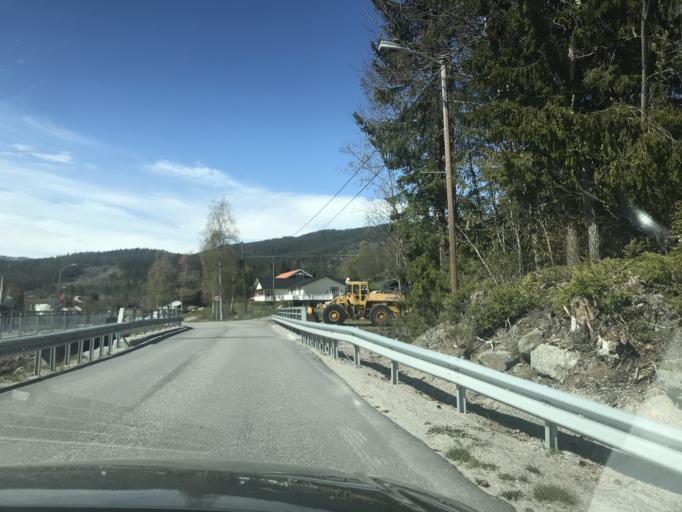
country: NO
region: Telemark
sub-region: Hjartdal
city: Sauland
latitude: 59.7547
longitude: 8.7944
